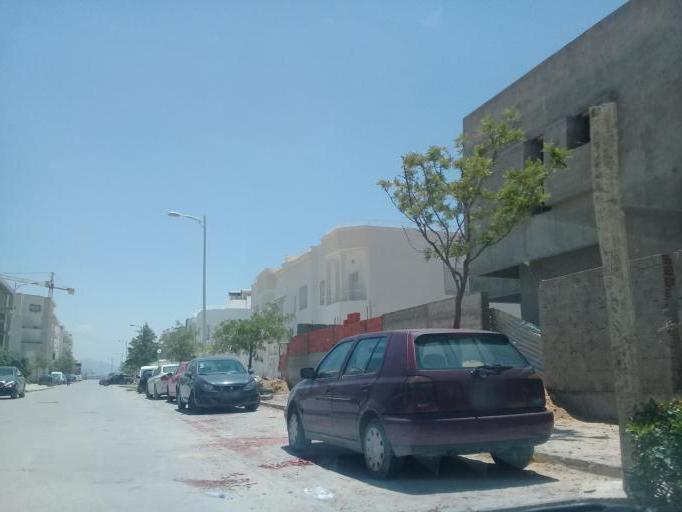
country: TN
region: Tunis
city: La Goulette
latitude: 36.8452
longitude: 10.2752
